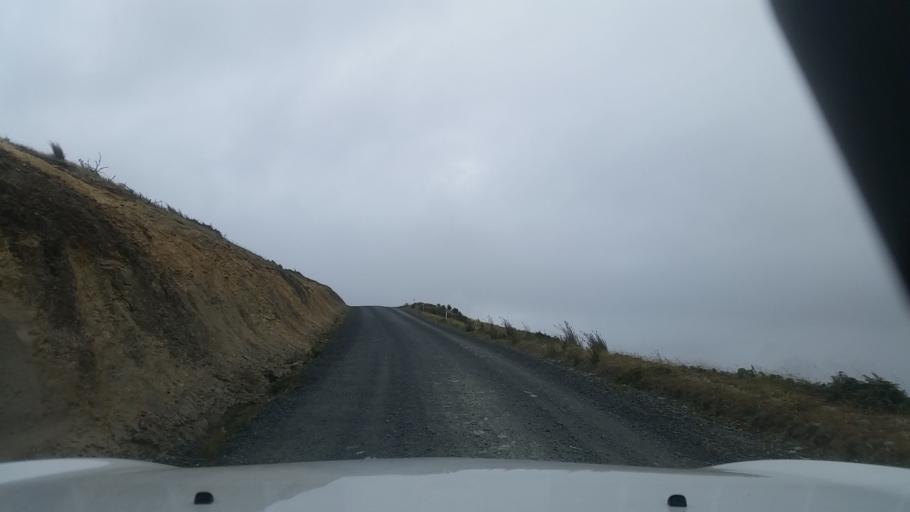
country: NZ
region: Chatham Islands
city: Waitangi
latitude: -43.8012
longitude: -176.6939
